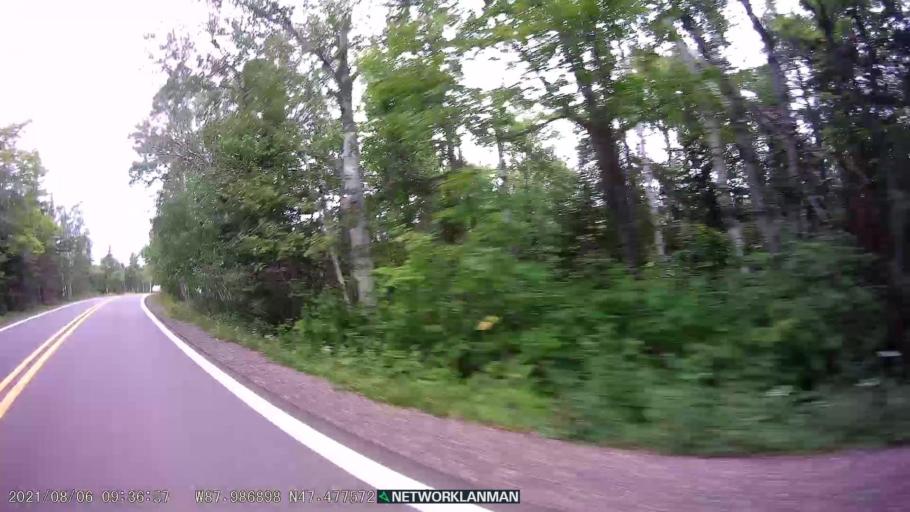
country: US
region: Michigan
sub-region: Keweenaw County
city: Eagle River
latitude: 47.4775
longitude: -87.9881
